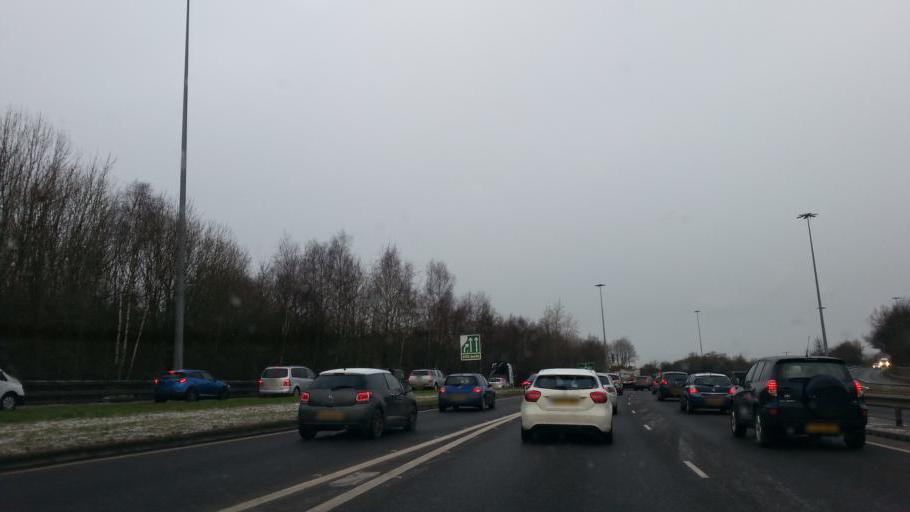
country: GB
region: England
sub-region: Rotherham
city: Orgreave
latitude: 53.3745
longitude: -1.4103
